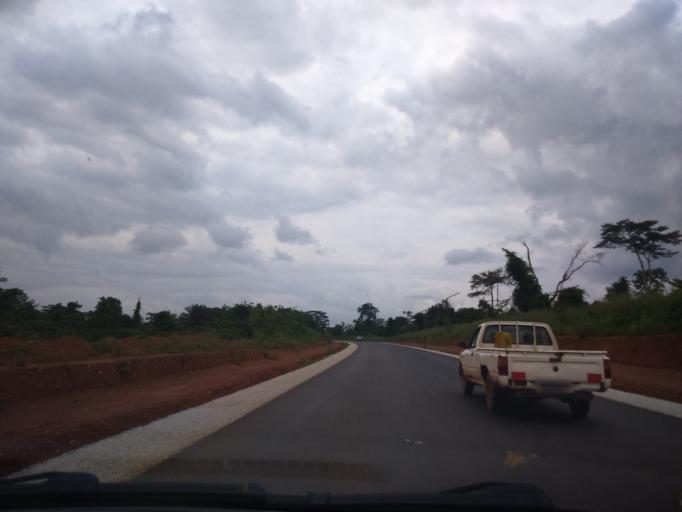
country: CI
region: Lagunes
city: Akoupe
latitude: 6.3207
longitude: -3.8330
